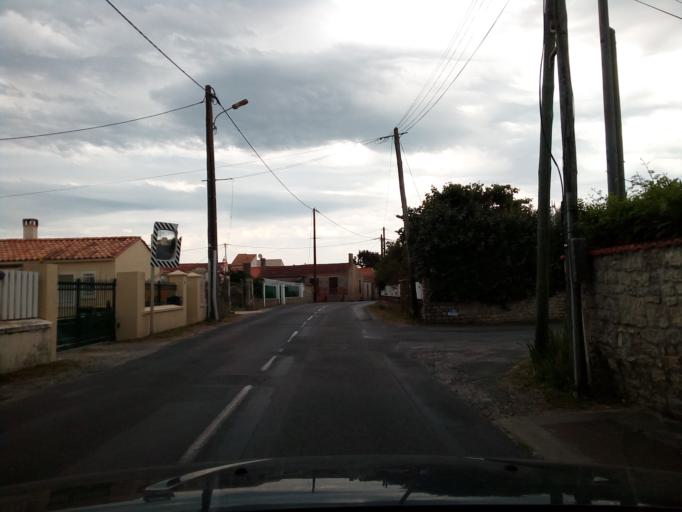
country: FR
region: Poitou-Charentes
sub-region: Departement de la Charente-Maritime
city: Dolus-d'Oleron
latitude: 45.9248
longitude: -1.3235
